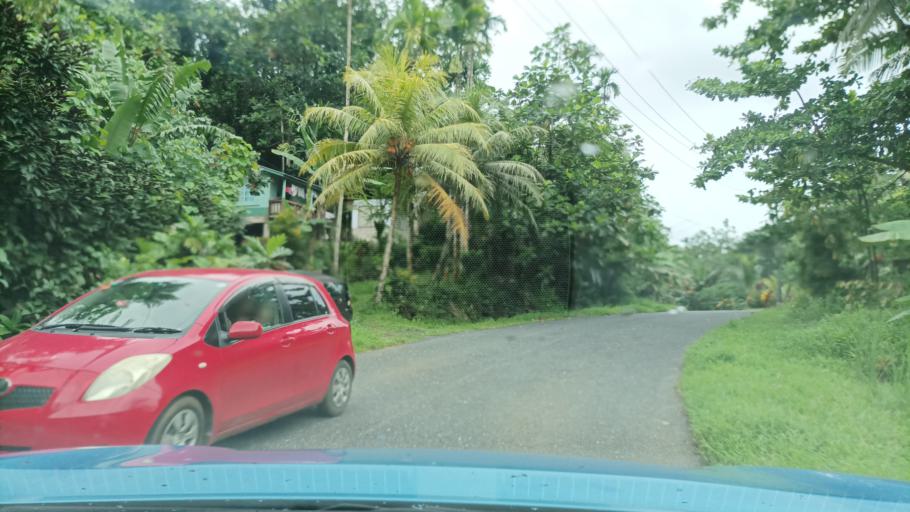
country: FM
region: Pohnpei
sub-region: Kolonia Municipality
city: Kolonia
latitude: 6.9479
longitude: 158.2744
